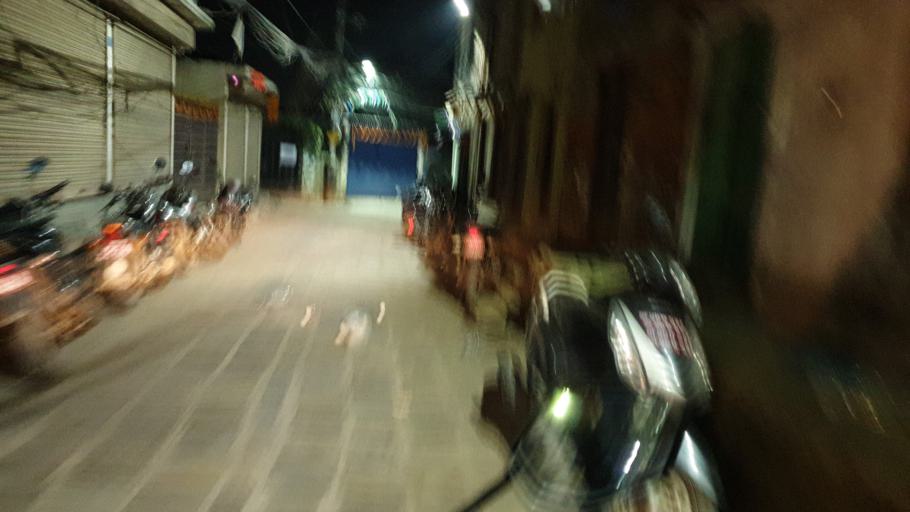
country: NP
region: Central Region
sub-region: Bagmati Zone
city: Kathmandu
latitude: 27.6984
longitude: 85.3079
